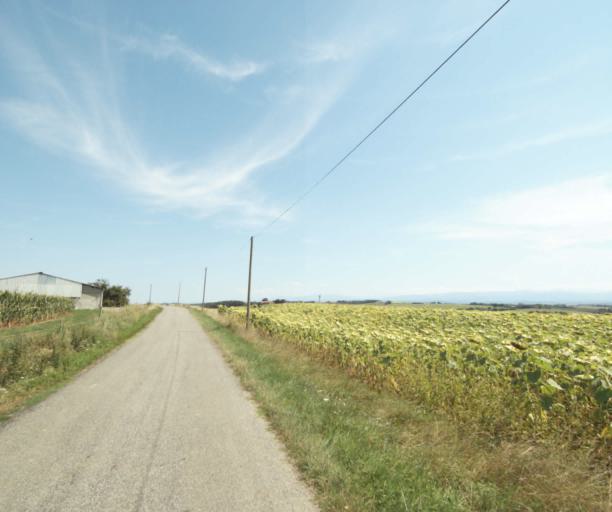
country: FR
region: Midi-Pyrenees
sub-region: Departement de la Haute-Garonne
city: Gaillac-Toulza
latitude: 43.2463
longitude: 1.4216
